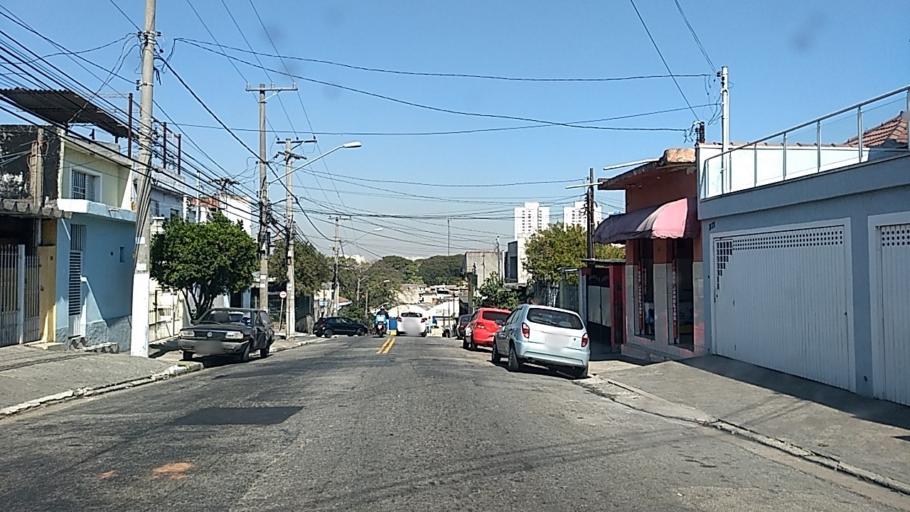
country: BR
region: Sao Paulo
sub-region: Guarulhos
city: Guarulhos
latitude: -23.5037
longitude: -46.5717
